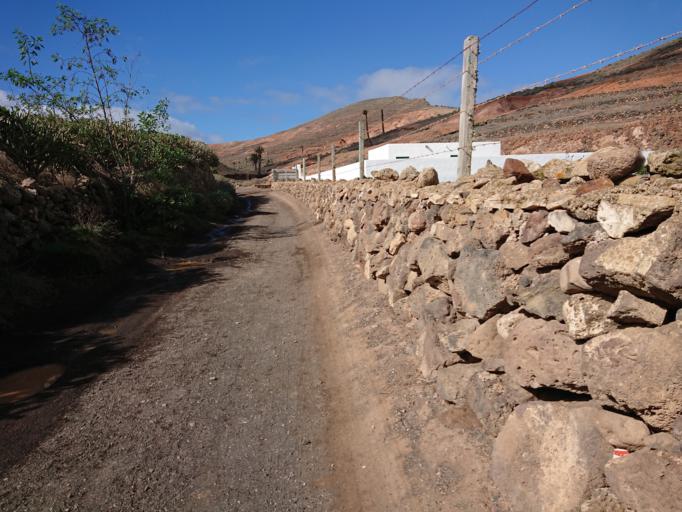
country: ES
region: Canary Islands
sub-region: Provincia de Las Palmas
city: Haria
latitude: 29.1447
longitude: -13.5109
